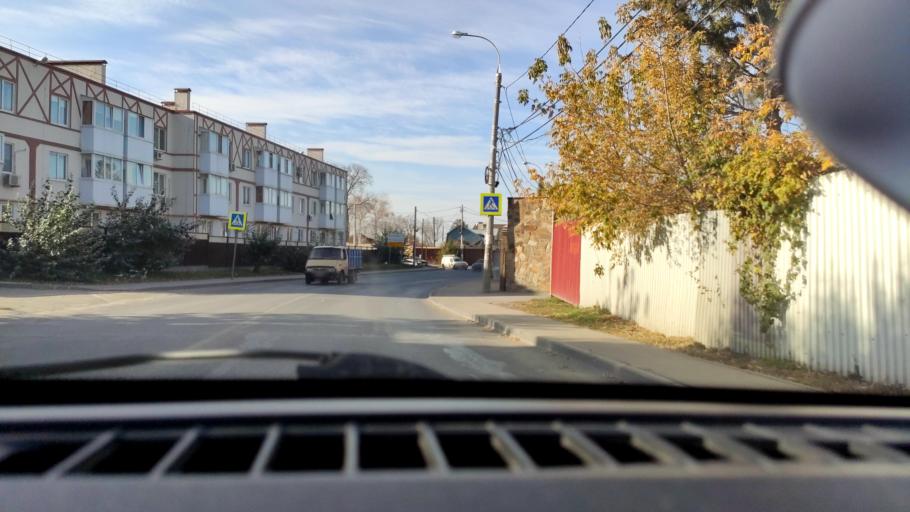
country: RU
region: Samara
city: Samara
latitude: 53.2674
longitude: 50.1988
